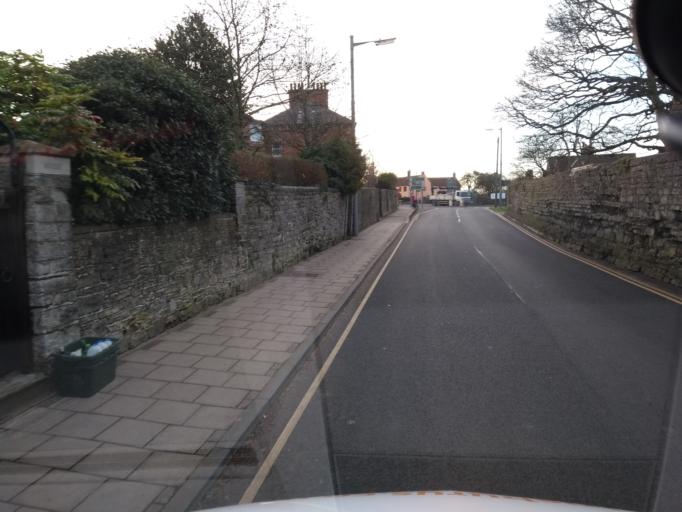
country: GB
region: England
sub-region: Somerset
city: Glastonbury
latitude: 51.1452
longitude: -2.7109
